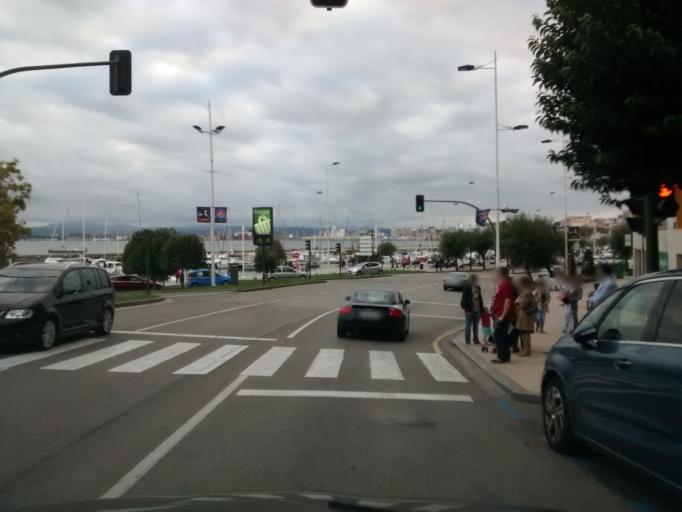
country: ES
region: Cantabria
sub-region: Provincia de Cantabria
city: Santander
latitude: 43.4631
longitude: -3.7914
